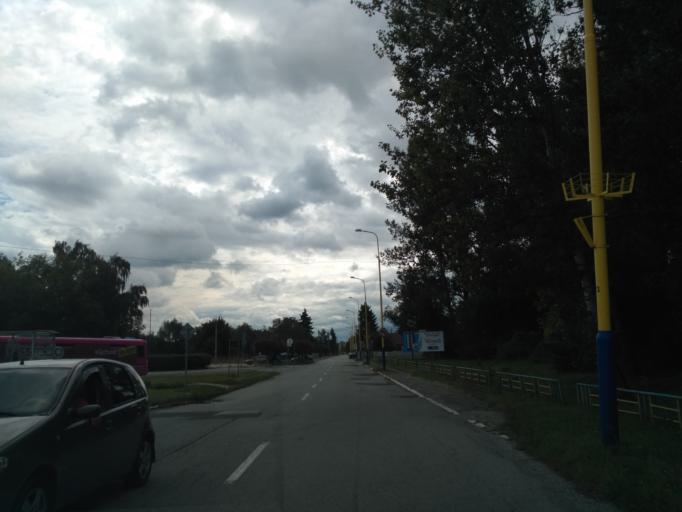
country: SK
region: Kosicky
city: Kosice
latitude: 48.6428
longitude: 21.1703
